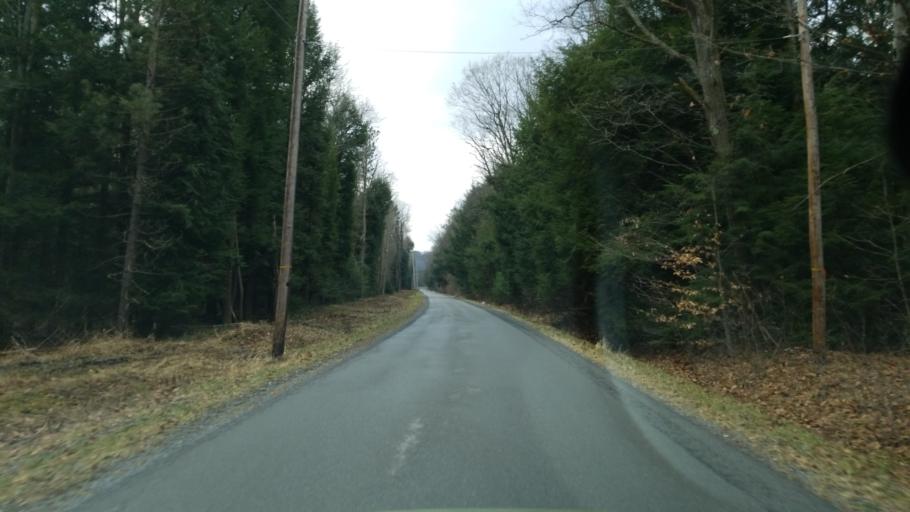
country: US
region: Pennsylvania
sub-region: Clearfield County
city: Treasure Lake
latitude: 41.1479
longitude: -78.5641
